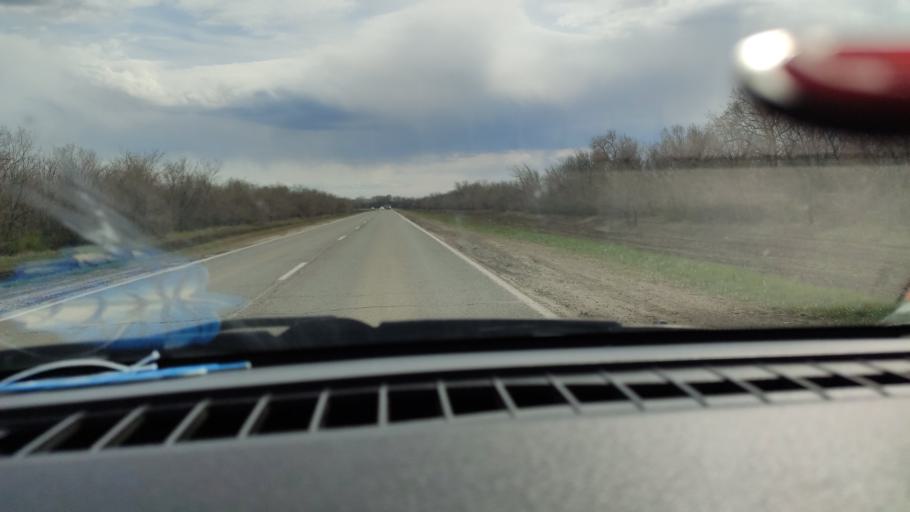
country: RU
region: Saratov
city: Privolzhskiy
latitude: 51.3554
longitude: 46.0436
